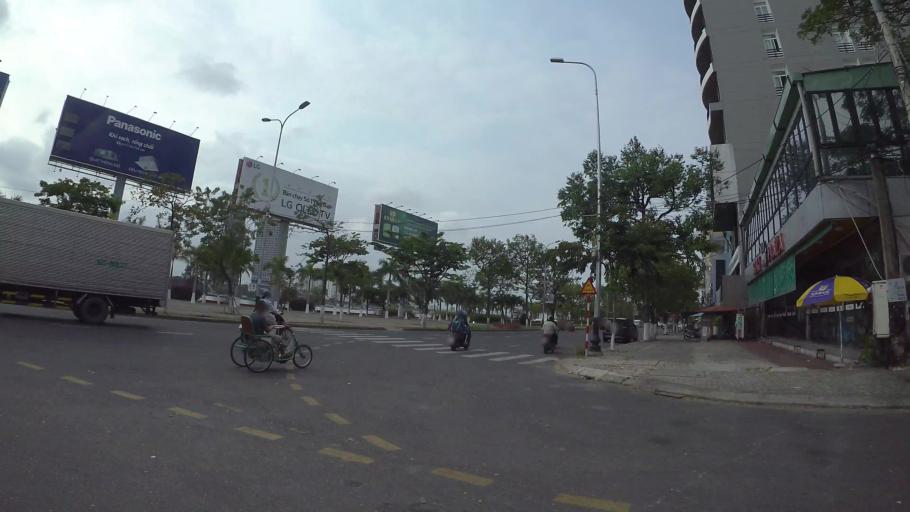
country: VN
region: Da Nang
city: Da Nang
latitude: 16.0741
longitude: 108.2291
